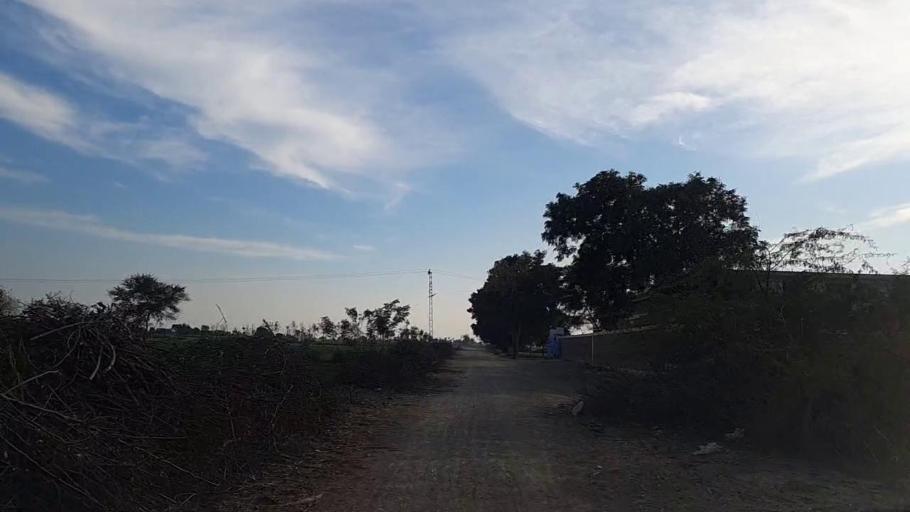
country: PK
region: Sindh
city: Bandhi
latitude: 26.5603
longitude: 68.2785
